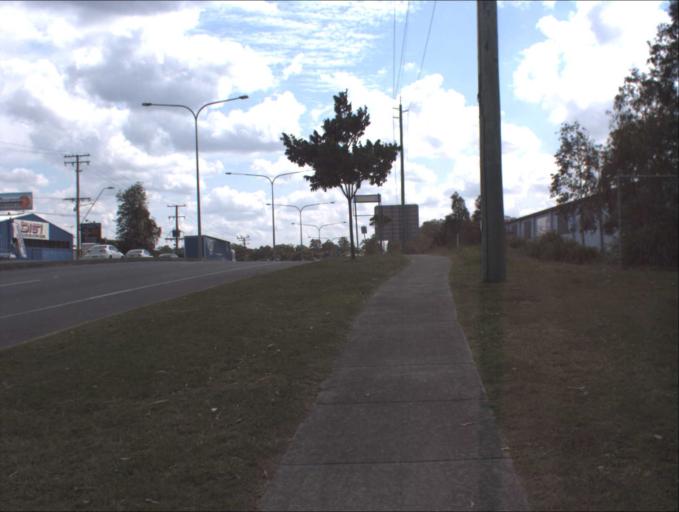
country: AU
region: Queensland
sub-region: Brisbane
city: Sunnybank Hills
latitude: -27.6596
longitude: 153.0351
